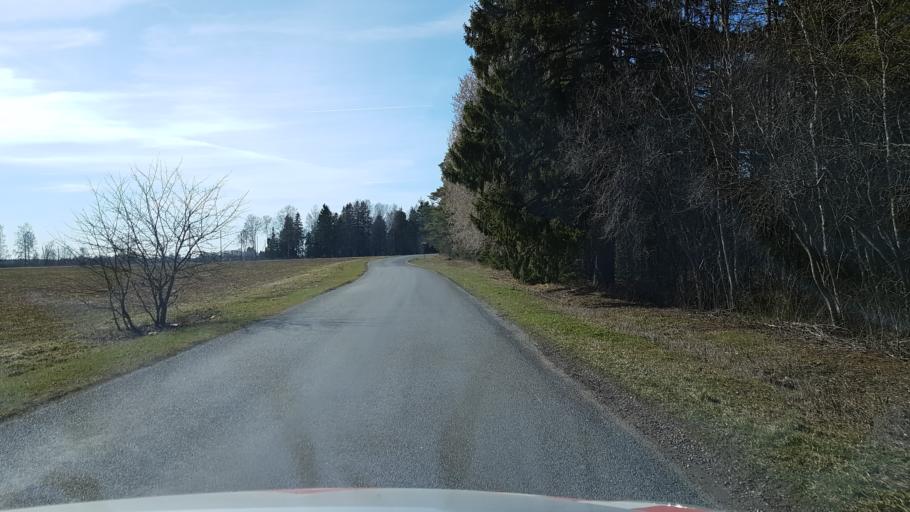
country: EE
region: Harju
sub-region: Nissi vald
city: Riisipere
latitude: 59.0989
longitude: 24.3277
